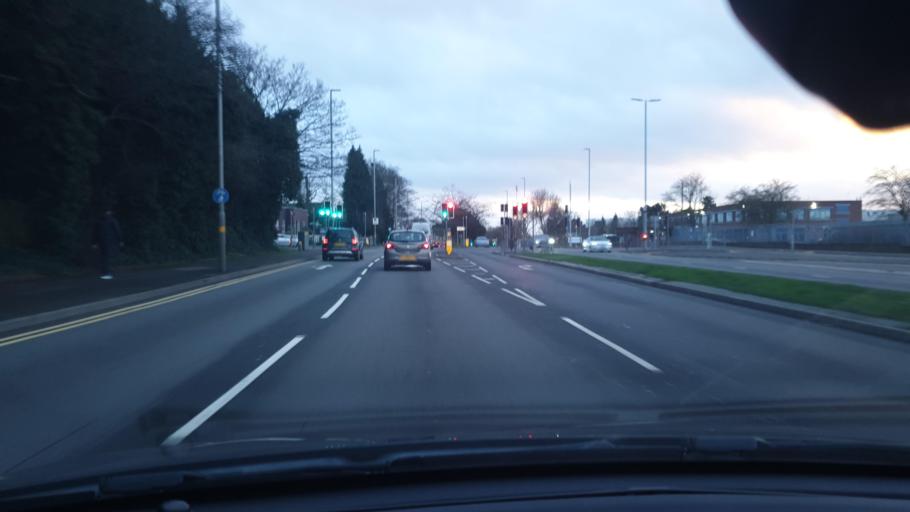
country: GB
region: England
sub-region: Staffordshire
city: Featherstone
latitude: 52.6326
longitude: -2.1249
